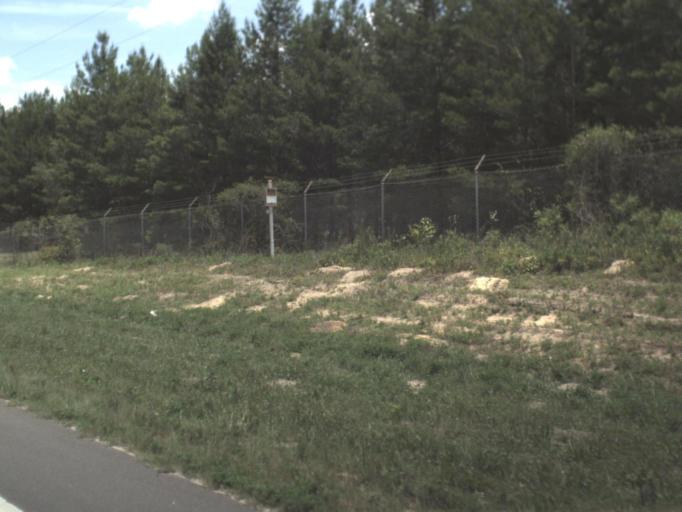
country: US
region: Florida
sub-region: Alachua County
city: Archer
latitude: 29.5193
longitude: -82.5451
